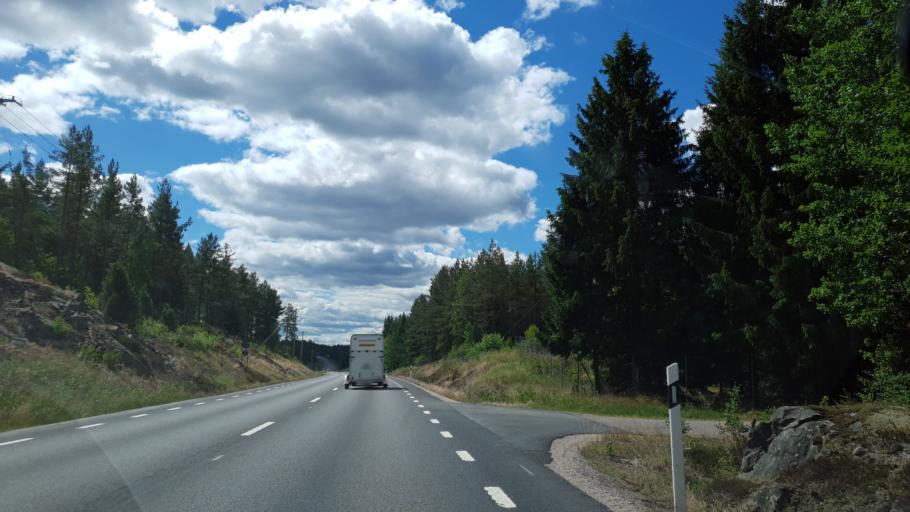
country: SE
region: Kronoberg
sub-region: Vaxjo Kommun
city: Braas
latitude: 57.1928
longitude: 15.1562
